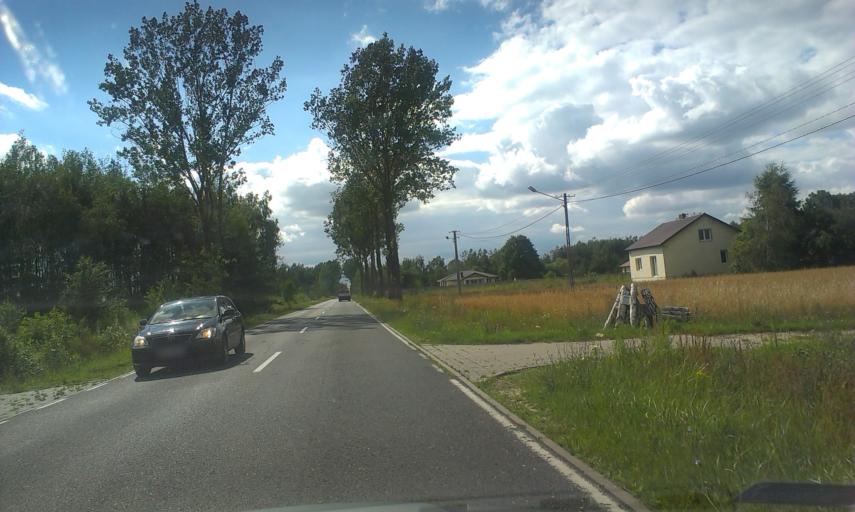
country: PL
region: Lodz Voivodeship
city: Zabia Wola
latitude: 51.9664
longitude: 20.6636
